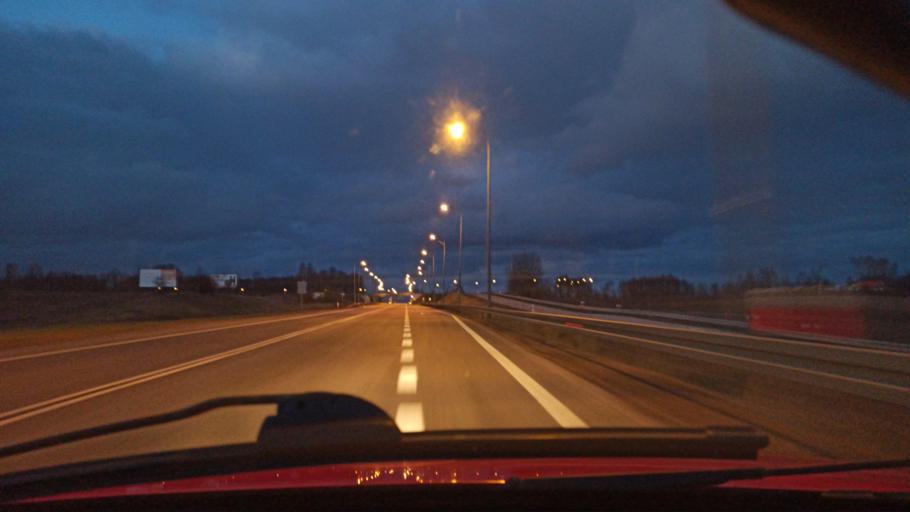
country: PL
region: Warmian-Masurian Voivodeship
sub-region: Powiat elblaski
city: Gronowo Gorne
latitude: 54.1664
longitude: 19.5251
